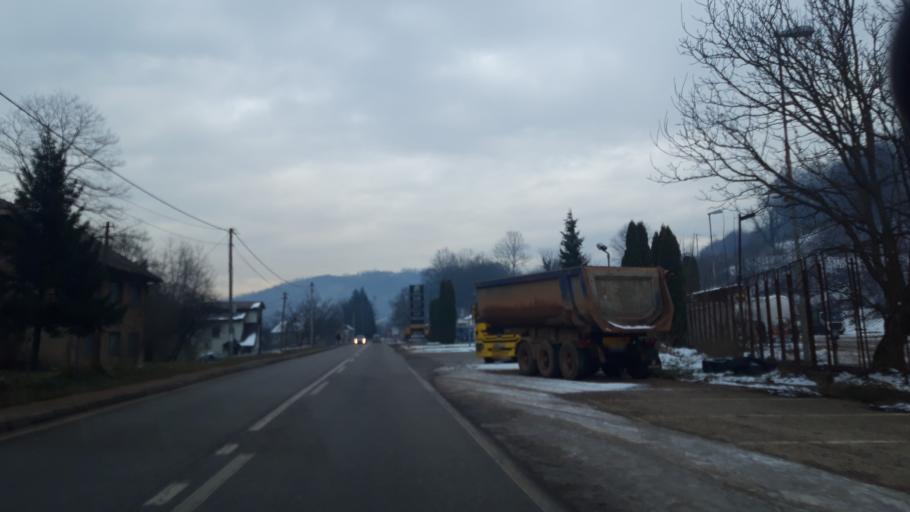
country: BA
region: Republika Srpska
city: Milici
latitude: 44.1752
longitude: 19.0751
